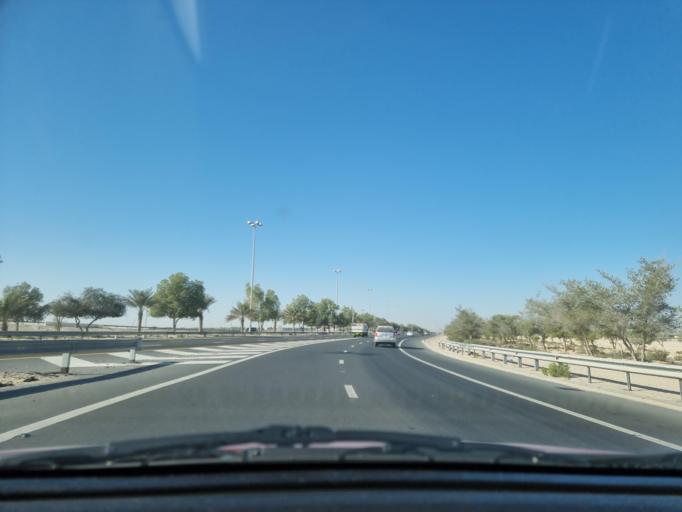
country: AE
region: Abu Dhabi
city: Abu Dhabi
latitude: 24.4144
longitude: 54.7103
